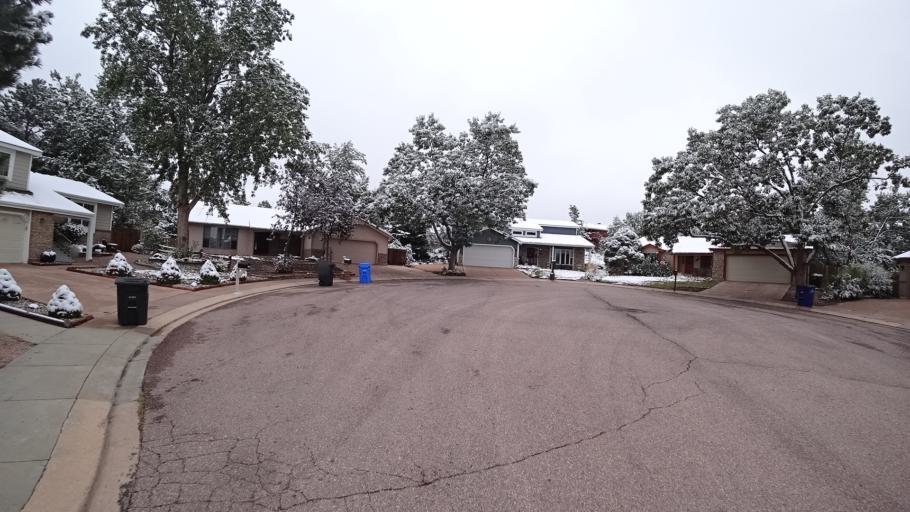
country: US
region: Colorado
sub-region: El Paso County
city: Colorado Springs
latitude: 38.9222
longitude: -104.7770
